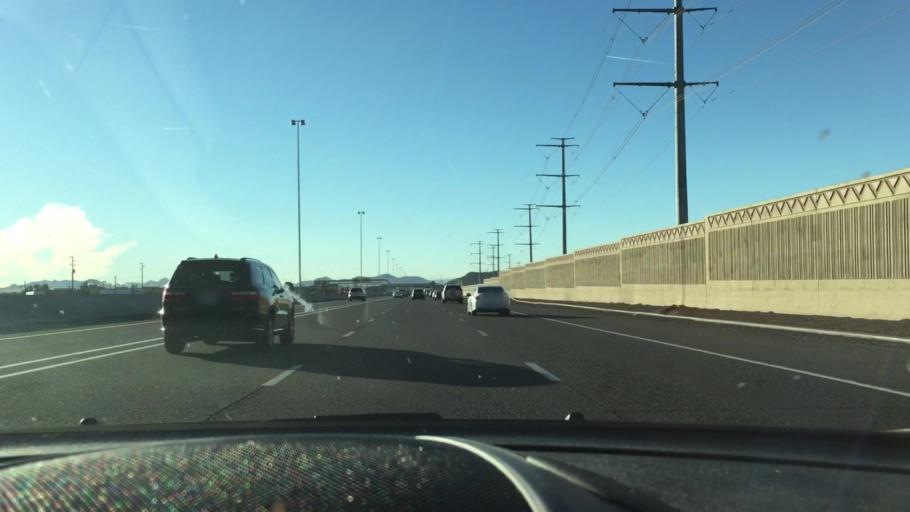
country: US
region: Arizona
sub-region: Maricopa County
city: Anthem
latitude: 33.7383
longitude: -112.1231
